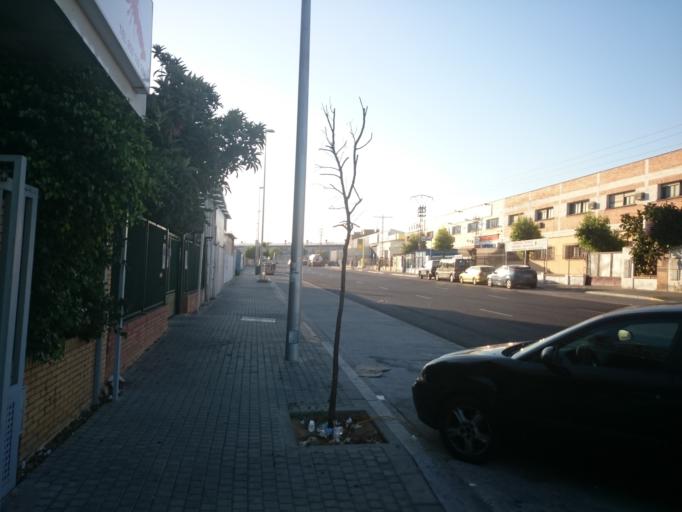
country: ES
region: Andalusia
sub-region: Provincia de Sevilla
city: Sevilla
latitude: 37.3897
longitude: -5.9520
